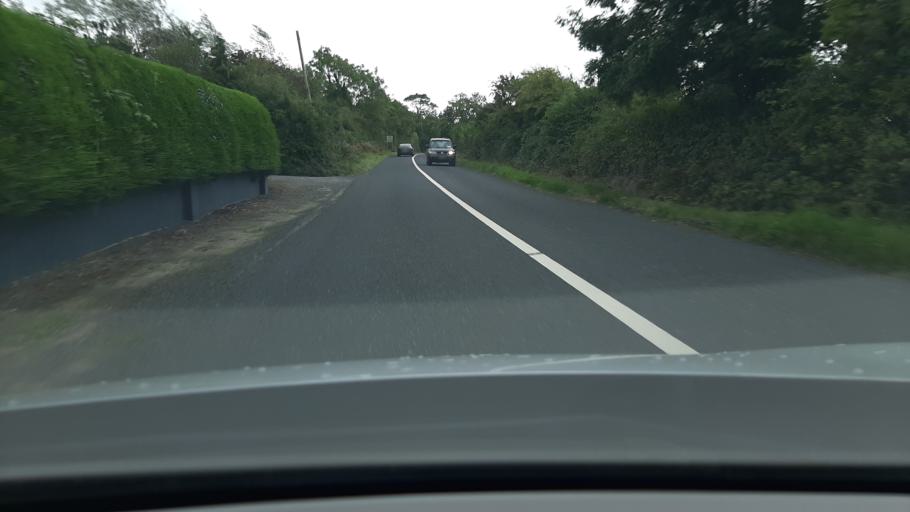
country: IE
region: Leinster
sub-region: Kildare
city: Rathangan
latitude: 53.2046
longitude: -6.9576
